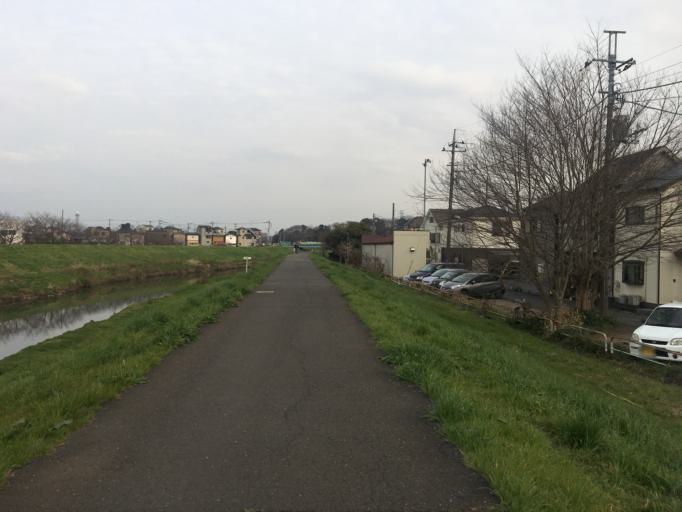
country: JP
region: Saitama
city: Shiki
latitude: 35.8490
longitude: 139.5630
